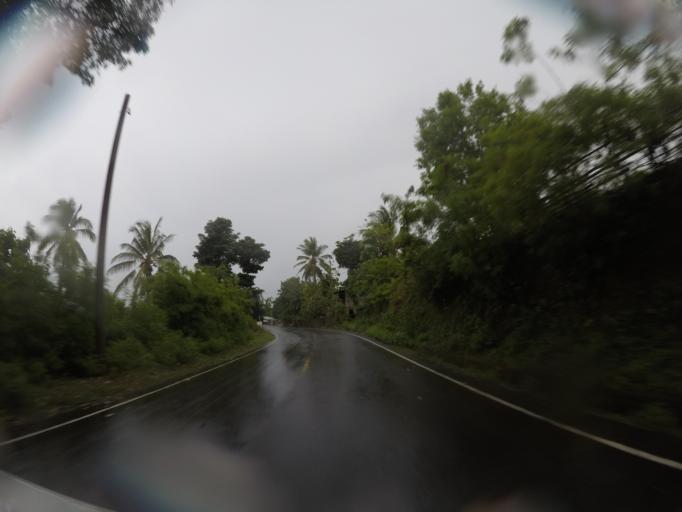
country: TL
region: Bobonaro
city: Maliana
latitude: -8.9531
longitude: 125.0698
